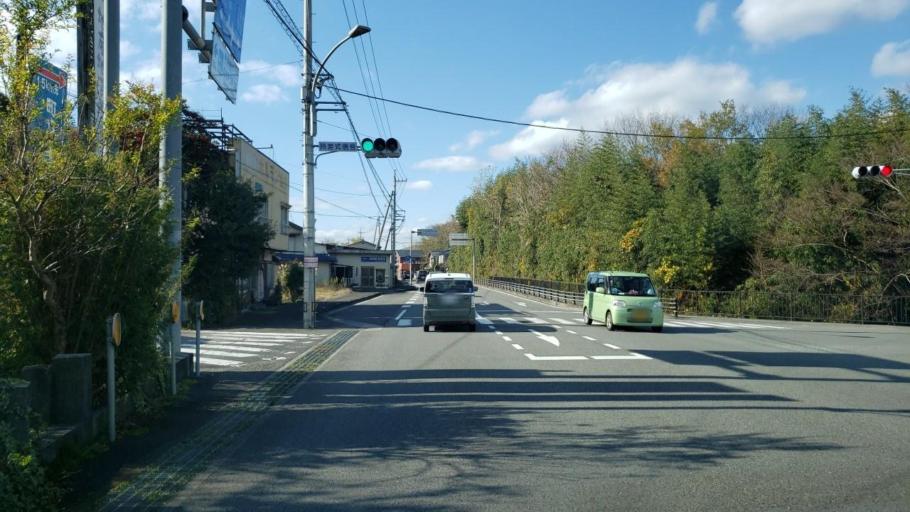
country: JP
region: Tokushima
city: Wakimachi
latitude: 34.0425
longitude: 134.0511
